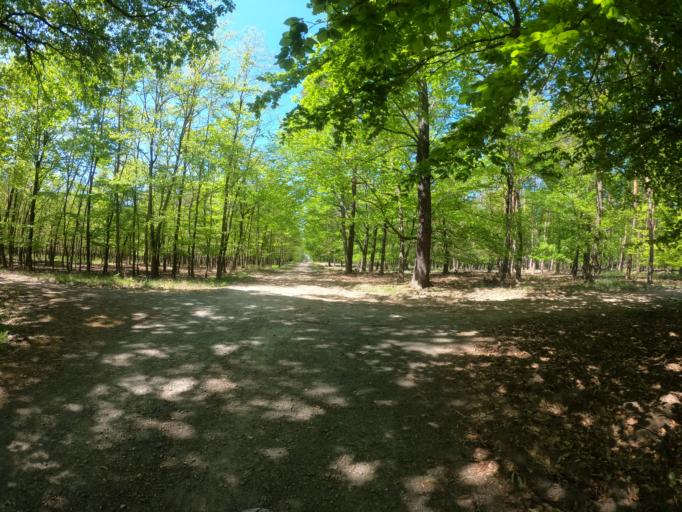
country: DE
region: Hesse
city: Kelsterbach
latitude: 50.0266
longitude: 8.5115
